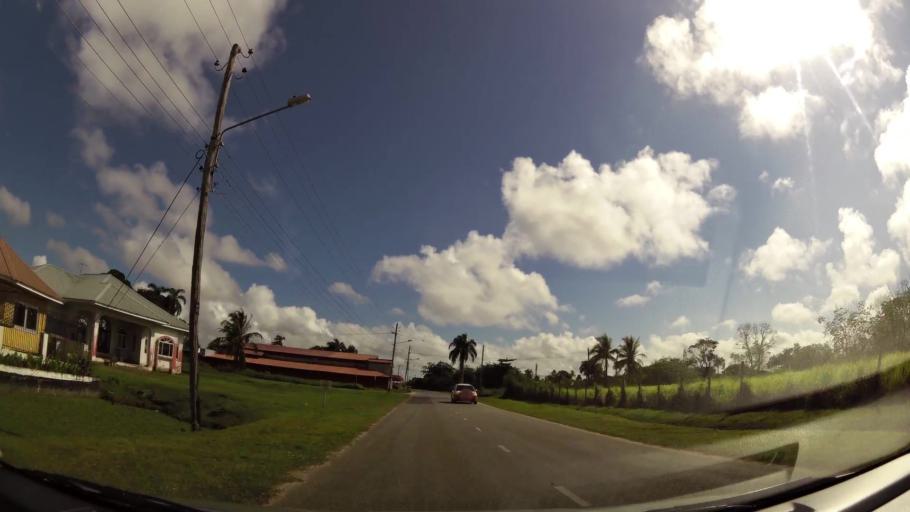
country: SR
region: Commewijne
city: Nieuw Amsterdam
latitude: 5.8667
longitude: -55.1005
